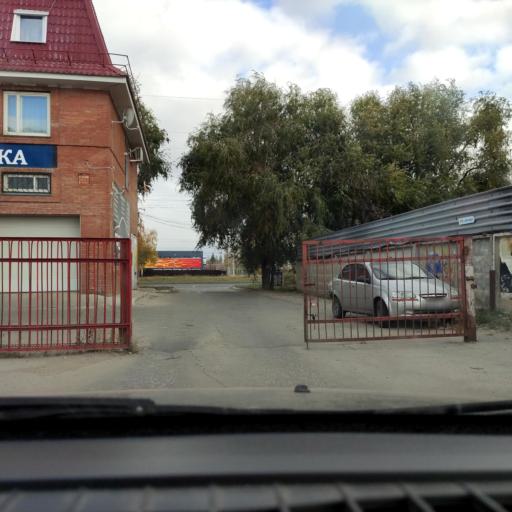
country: RU
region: Samara
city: Tol'yatti
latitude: 53.5435
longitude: 49.2634
